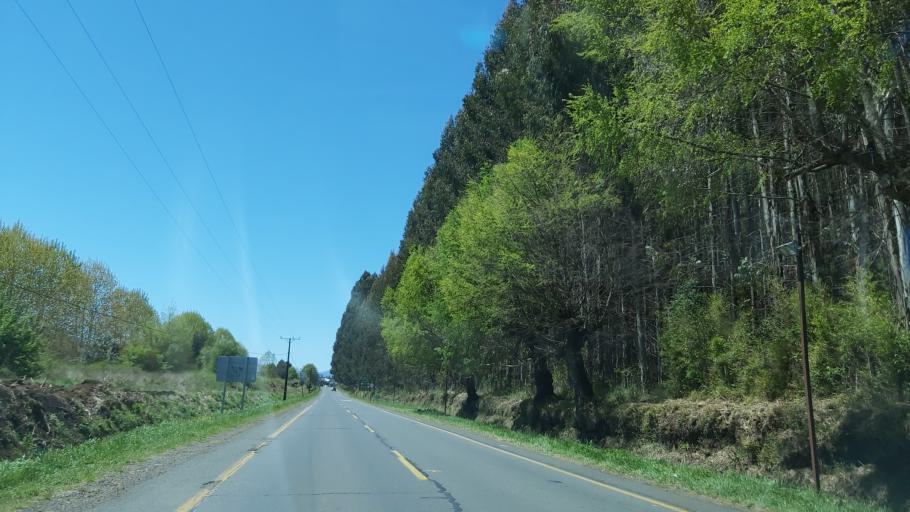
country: CL
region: Araucania
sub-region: Provincia de Cautin
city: Vilcun
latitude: -38.4334
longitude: -71.9081
